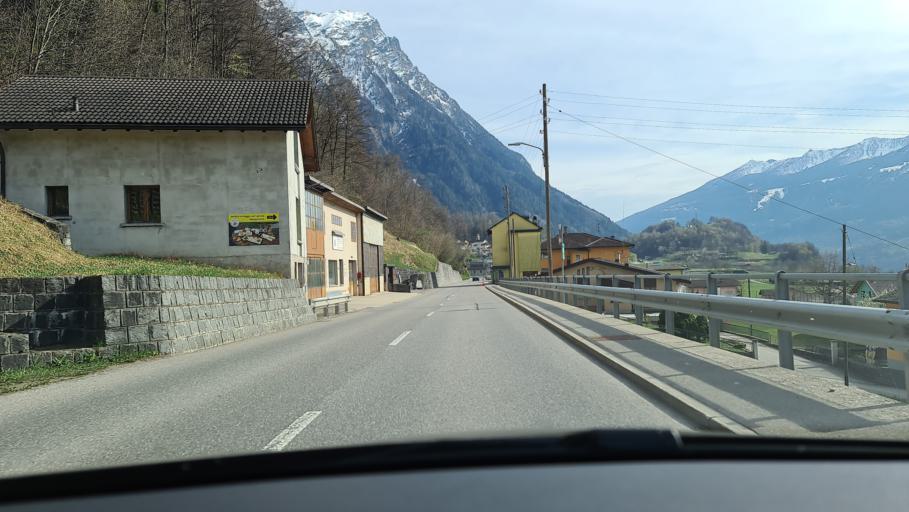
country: CH
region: Ticino
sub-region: Blenio District
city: Acquarossa
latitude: 46.5023
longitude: 8.9508
